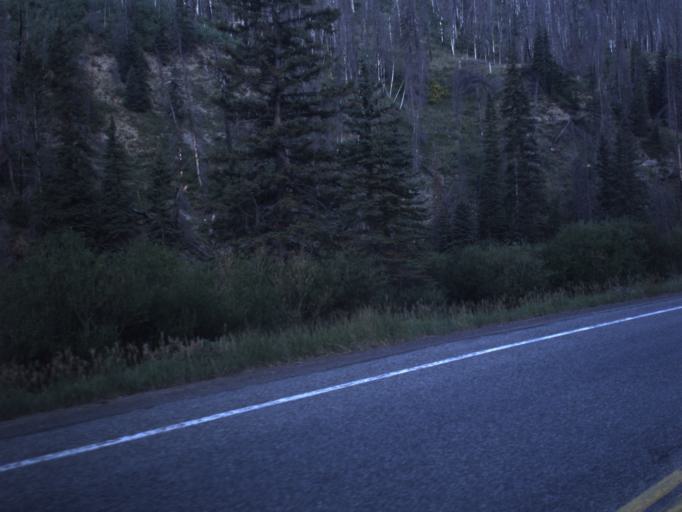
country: US
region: Utah
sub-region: Sanpete County
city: Fairview
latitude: 39.5640
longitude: -111.1771
